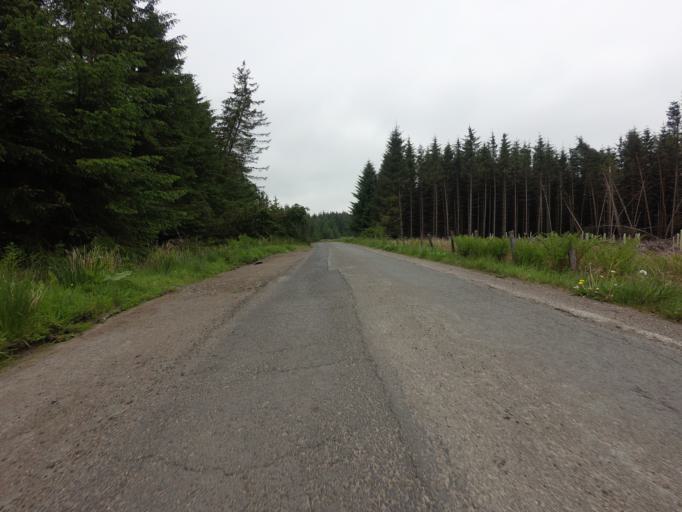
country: GB
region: Scotland
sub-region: Fife
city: Townhill
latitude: 56.1451
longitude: -3.4508
